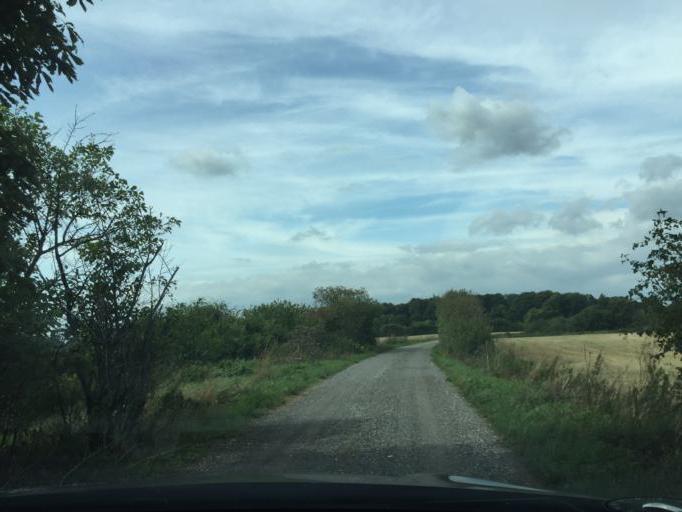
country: DK
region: South Denmark
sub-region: Assens Kommune
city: Vissenbjerg
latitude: 55.3613
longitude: 10.1511
